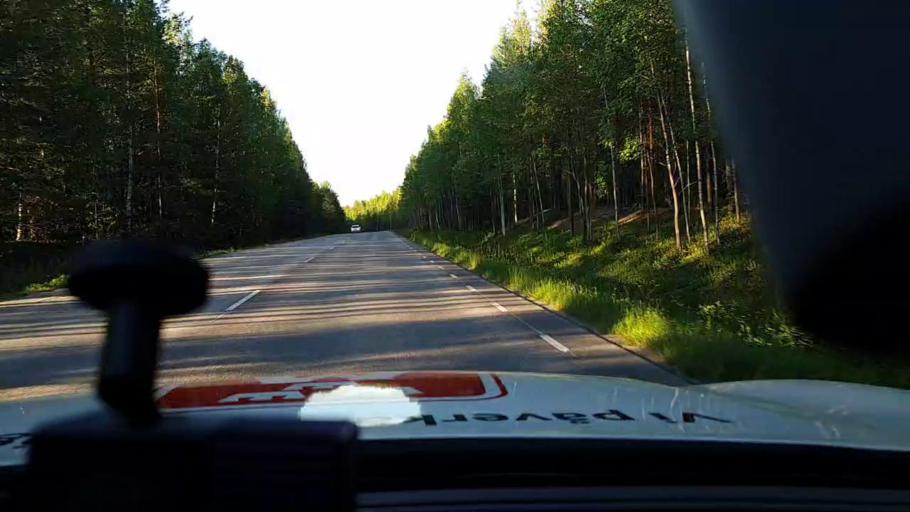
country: SE
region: Norrbotten
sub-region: Lulea Kommun
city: Lulea
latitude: 65.6134
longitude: 22.1932
